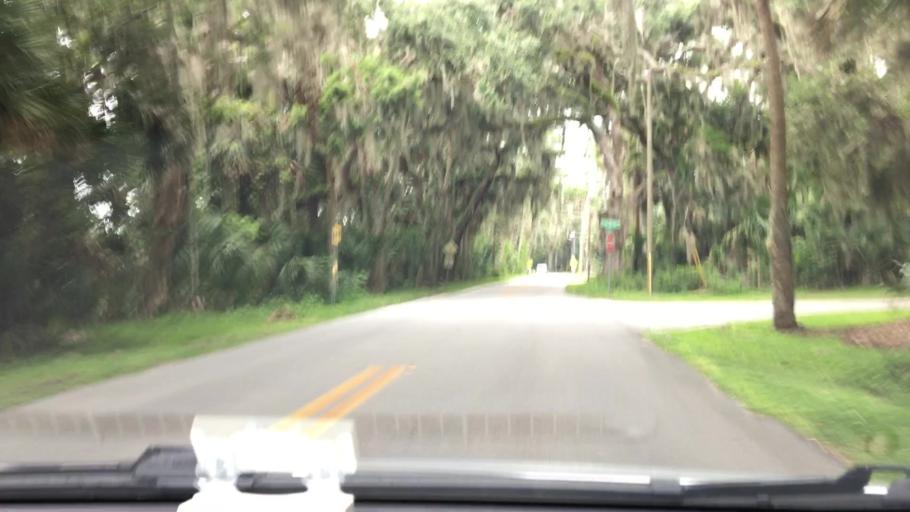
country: US
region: Florida
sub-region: Volusia County
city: Deltona
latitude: 28.8619
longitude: -81.2509
